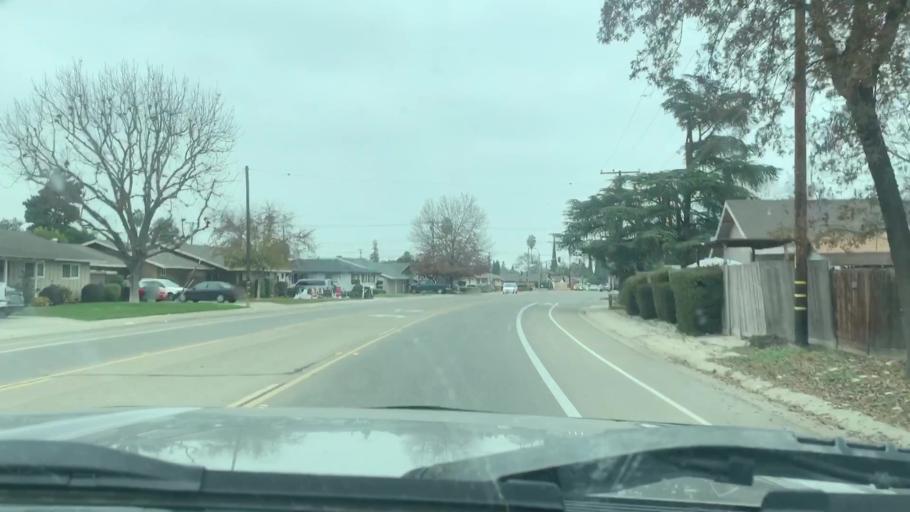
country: US
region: California
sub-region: Tulare County
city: Visalia
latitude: 36.3186
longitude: -119.3271
